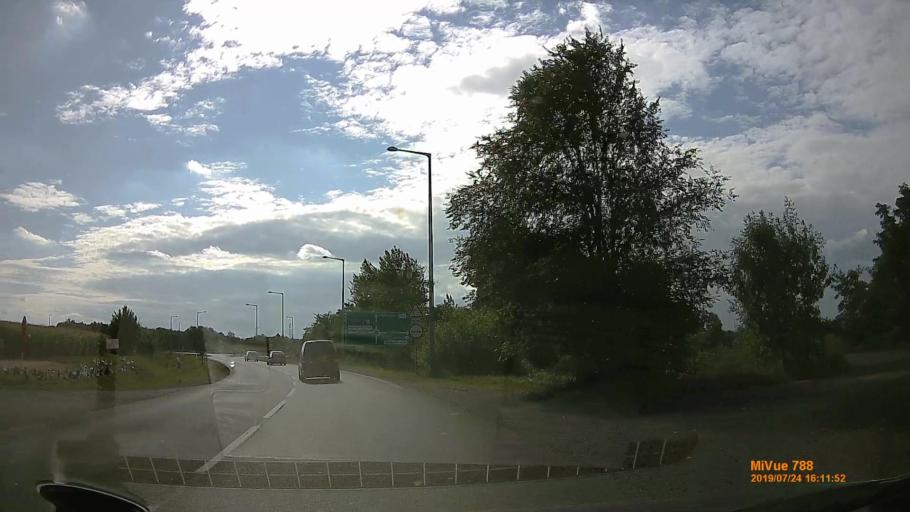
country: HU
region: Szabolcs-Szatmar-Bereg
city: Nyirpazony
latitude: 47.9512
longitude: 21.8226
